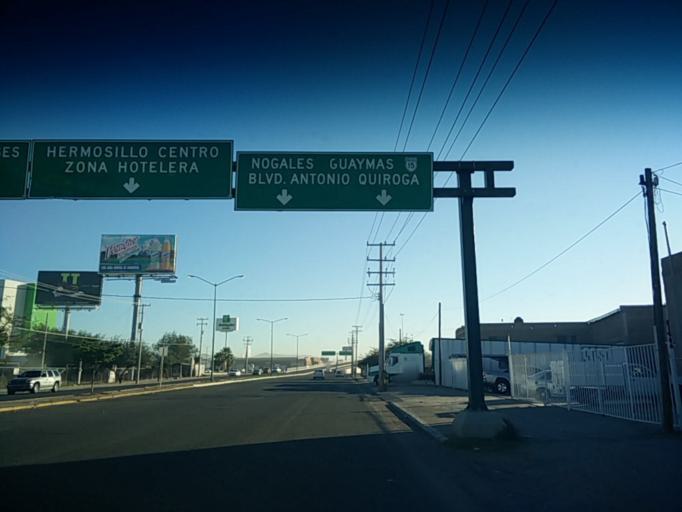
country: MX
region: Sonora
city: Hermosillo
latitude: 29.0947
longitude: -111.0270
